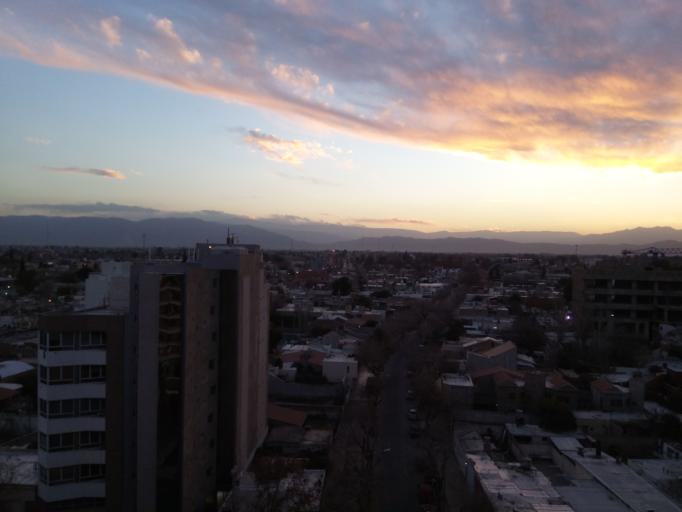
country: AR
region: San Juan
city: San Juan
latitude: -31.5370
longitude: -68.5389
